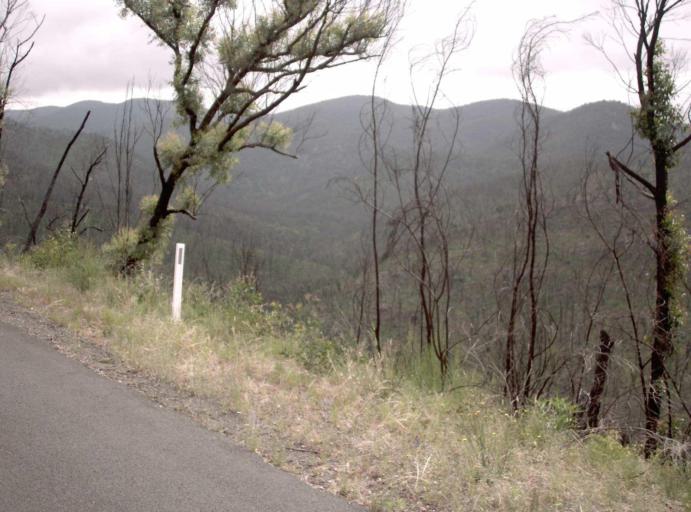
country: AU
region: Victoria
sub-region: Wellington
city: Heyfield
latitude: -37.7296
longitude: 146.6703
